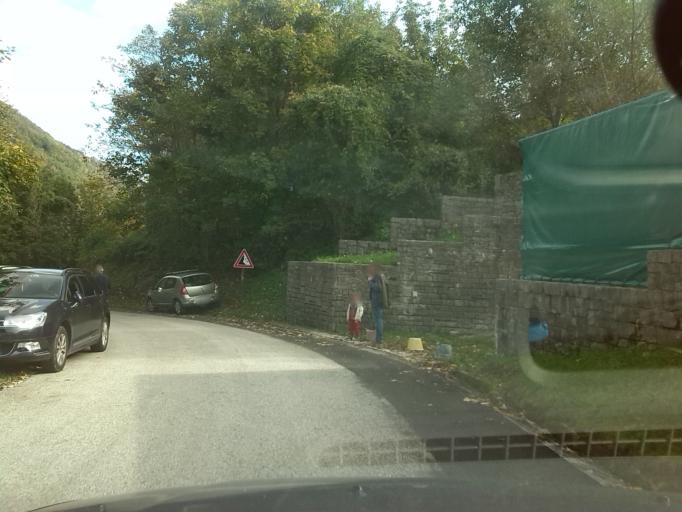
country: IT
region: Friuli Venezia Giulia
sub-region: Provincia di Udine
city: Clodig
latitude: 46.1432
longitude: 13.6161
